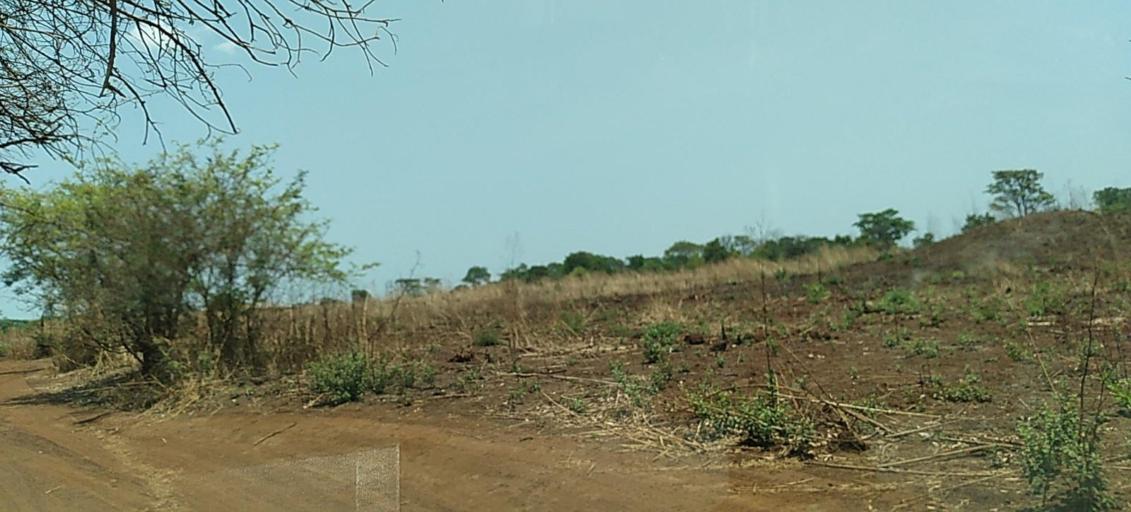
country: ZM
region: Copperbelt
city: Mpongwe
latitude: -13.8384
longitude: 27.8437
